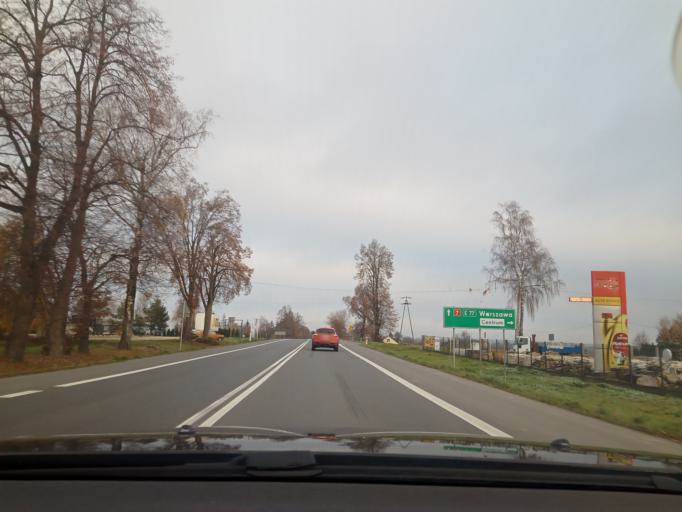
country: PL
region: Lesser Poland Voivodeship
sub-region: Powiat miechowski
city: Miechow
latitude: 50.3341
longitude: 20.0341
